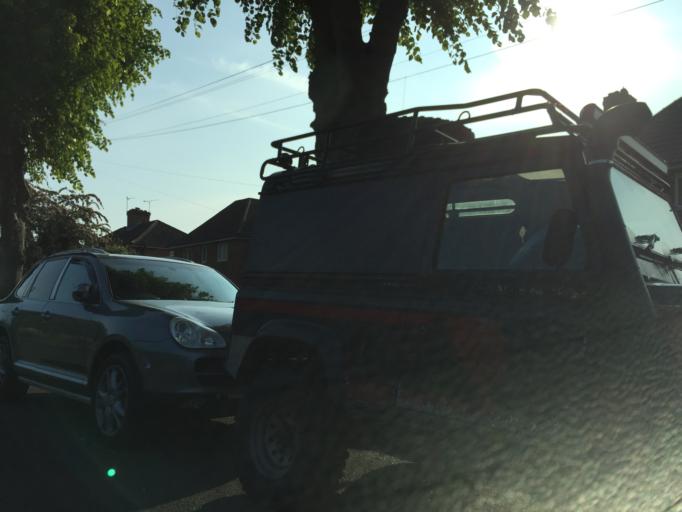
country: GB
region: England
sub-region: Bristol
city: Bristol
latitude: 51.5051
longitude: -2.6103
